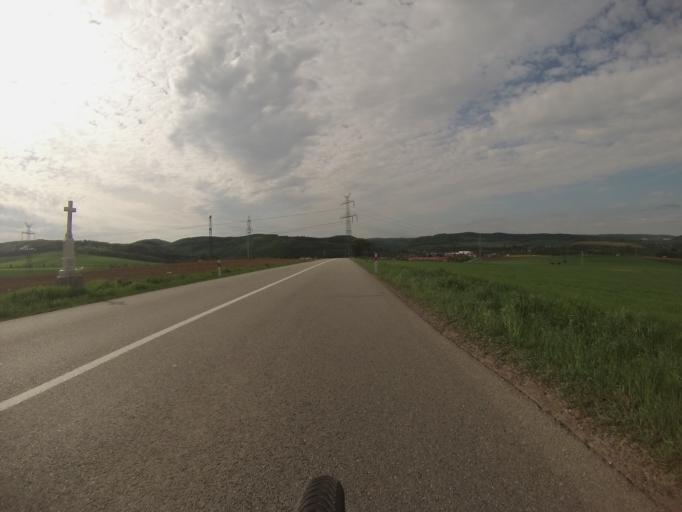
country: CZ
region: South Moravian
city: Veverska Bityska
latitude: 49.2621
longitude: 16.4426
